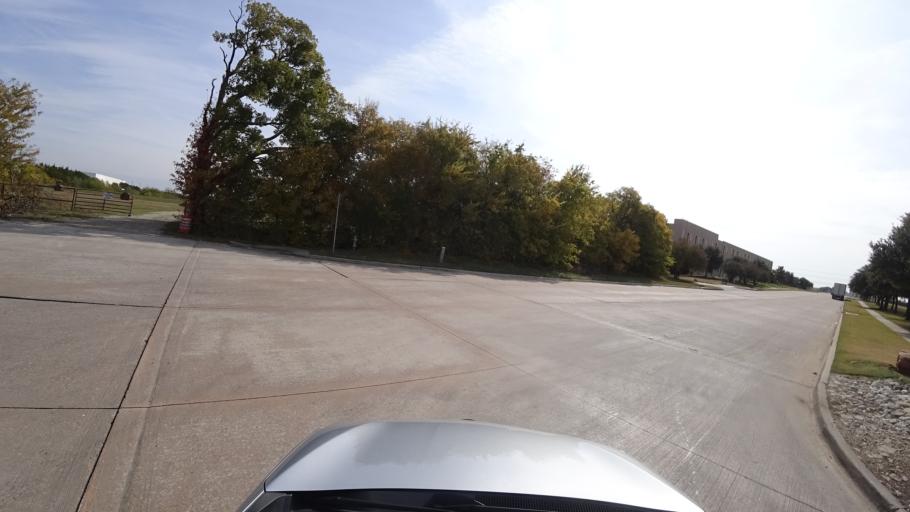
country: US
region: Texas
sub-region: Denton County
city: The Colony
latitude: 33.0656
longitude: -96.8714
